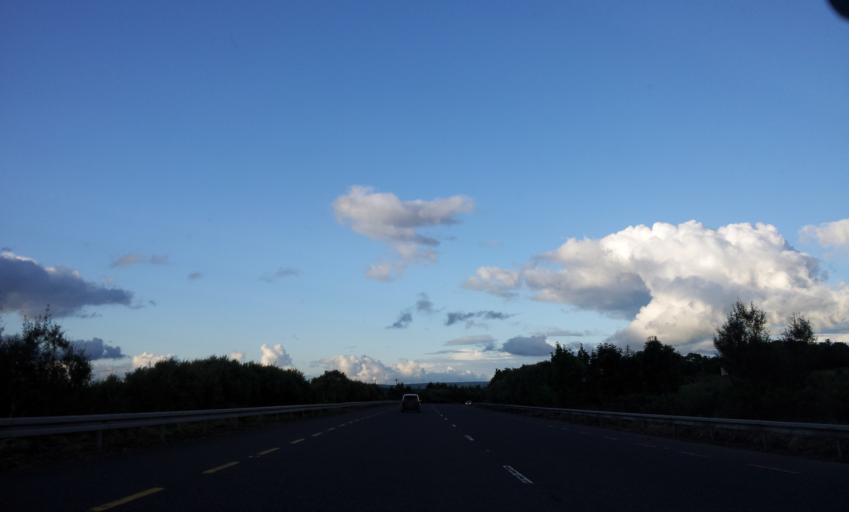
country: IE
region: Munster
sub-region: County Limerick
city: Abbeyfeale
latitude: 52.3376
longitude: -9.3534
